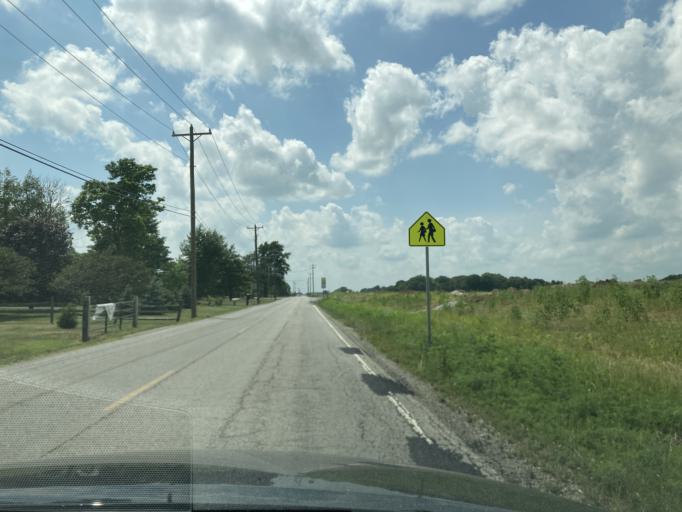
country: US
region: Indiana
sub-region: Boone County
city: Zionsville
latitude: 39.9990
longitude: -86.2091
